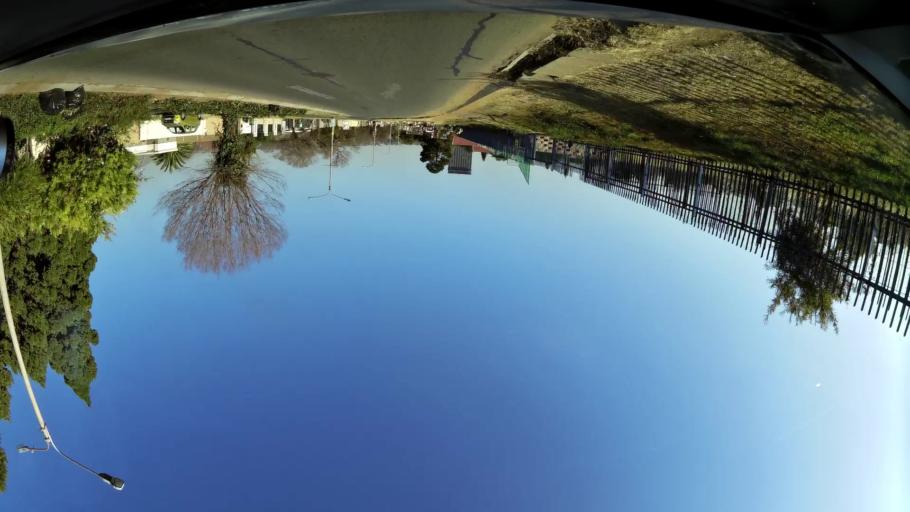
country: ZA
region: Gauteng
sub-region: City of Johannesburg Metropolitan Municipality
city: Modderfontein
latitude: -26.1543
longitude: 28.1531
